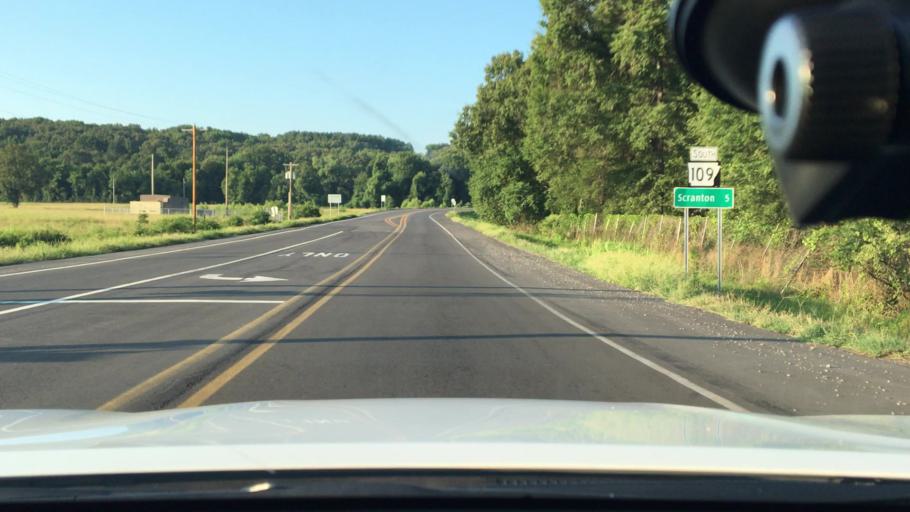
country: US
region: Arkansas
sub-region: Johnson County
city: Clarksville
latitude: 35.4258
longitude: -93.5296
